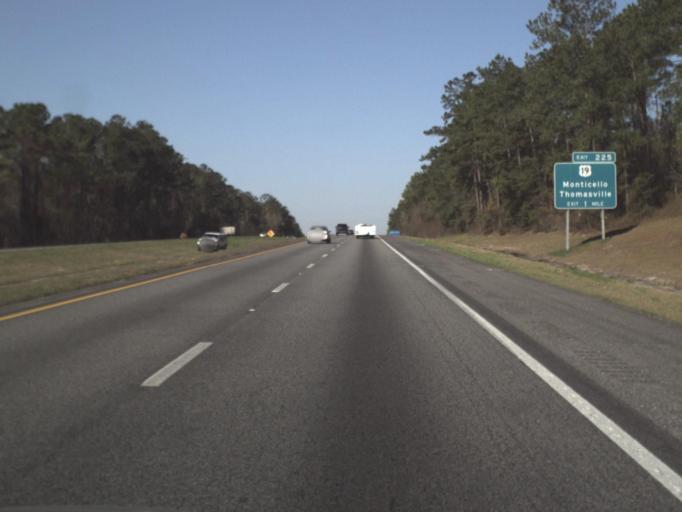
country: US
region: Florida
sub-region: Jefferson County
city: Monticello
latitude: 30.4735
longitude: -83.8678
